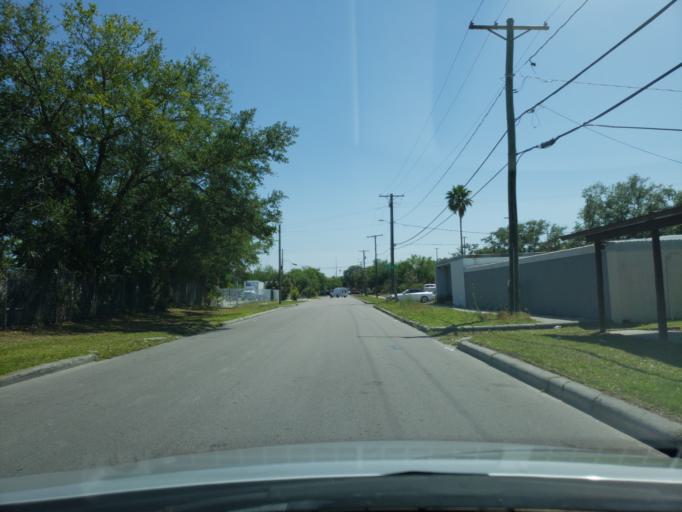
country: US
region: Florida
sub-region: Hillsborough County
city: Tampa
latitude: 27.9466
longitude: -82.4747
